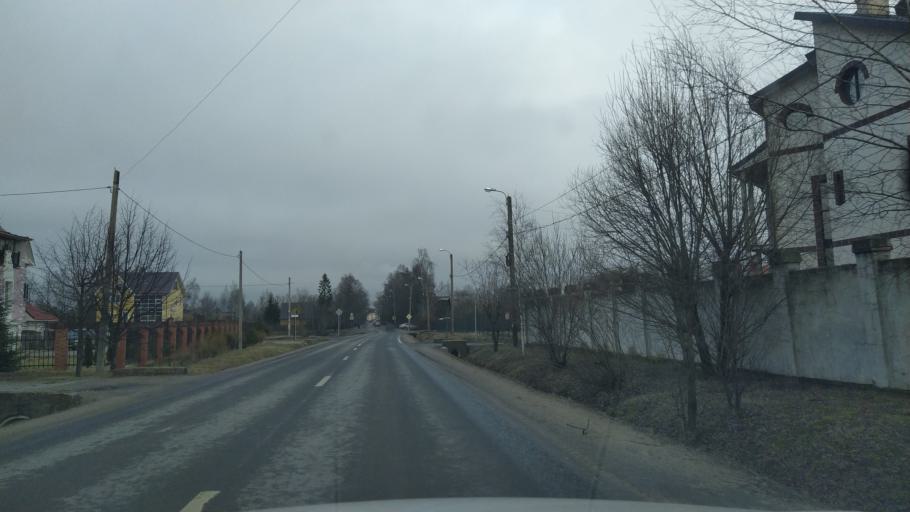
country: RU
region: St.-Petersburg
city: Aleksandrovskaya
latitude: 59.7249
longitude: 30.3501
